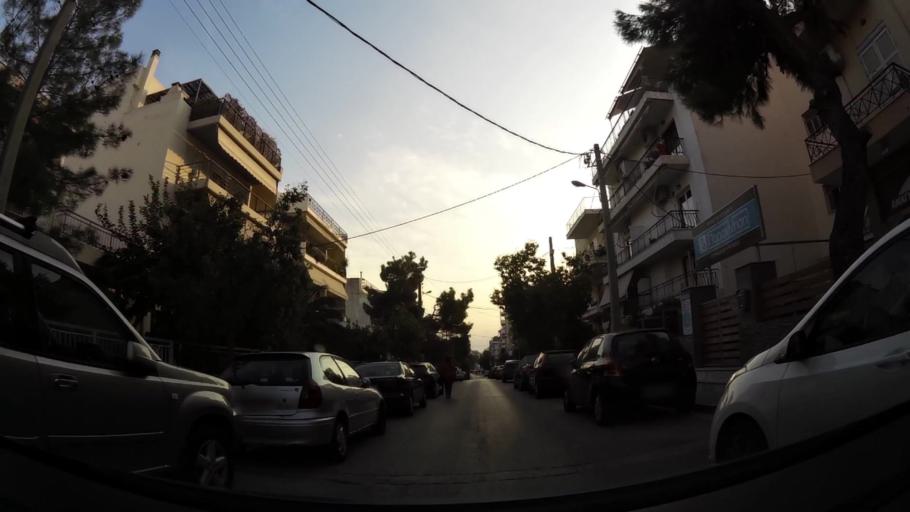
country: GR
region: Attica
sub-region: Nomarchia Athinas
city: Petroupolis
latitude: 38.0390
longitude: 23.6873
